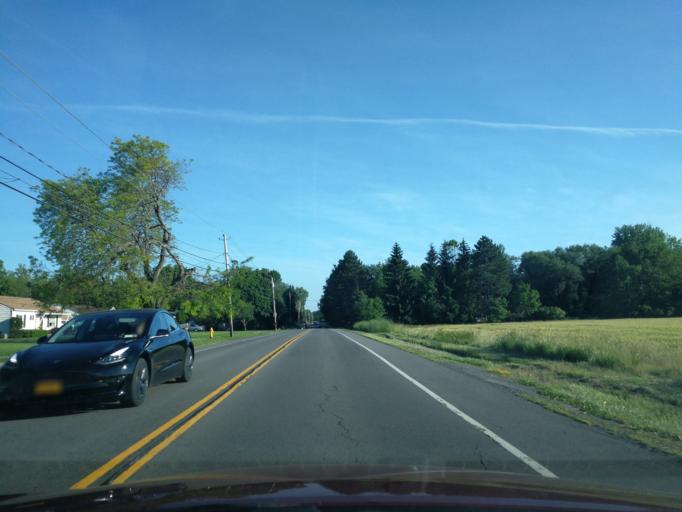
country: US
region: New York
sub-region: Monroe County
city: Greece
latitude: 43.2578
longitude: -77.7155
